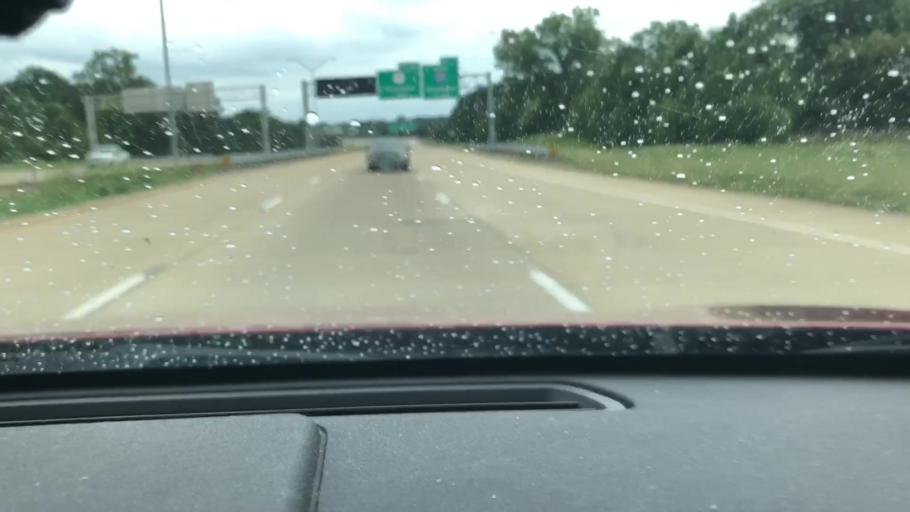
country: US
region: Texas
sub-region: Bowie County
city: Texarkana
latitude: 33.3855
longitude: -94.0382
